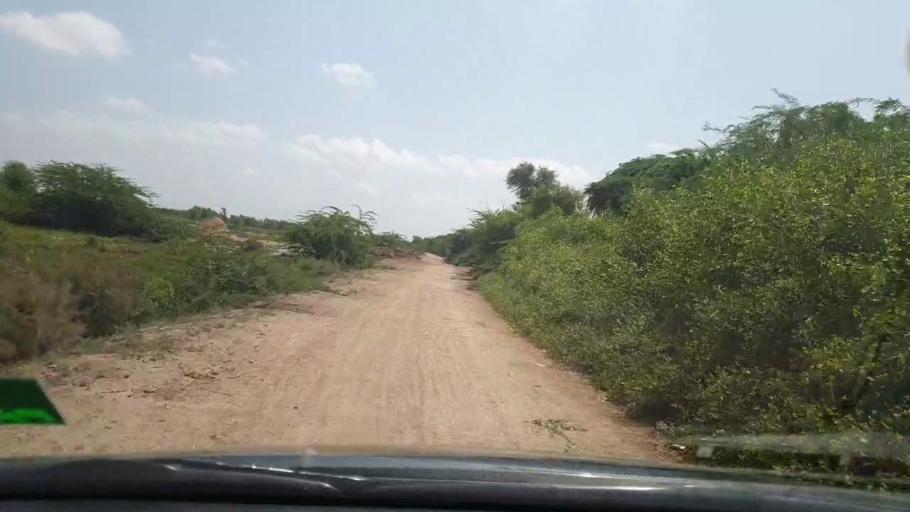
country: PK
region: Sindh
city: Tando Bago
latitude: 24.8545
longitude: 69.0891
